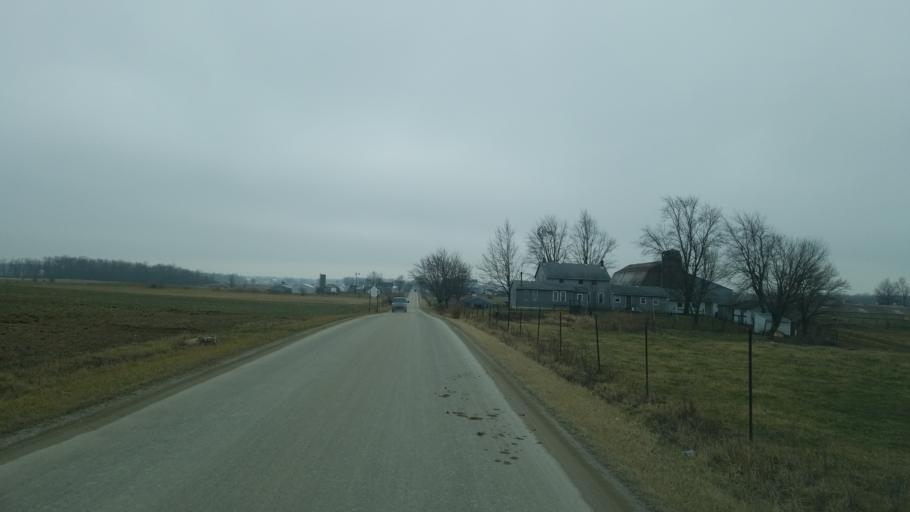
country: US
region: Indiana
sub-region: Adams County
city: Geneva
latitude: 40.6141
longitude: -84.9258
